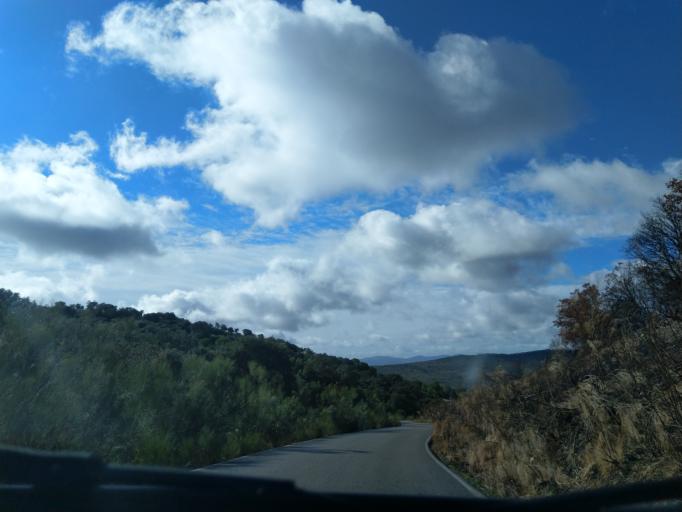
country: ES
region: Extremadura
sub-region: Provincia de Badajoz
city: Reina
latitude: 38.1464
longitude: -5.9133
